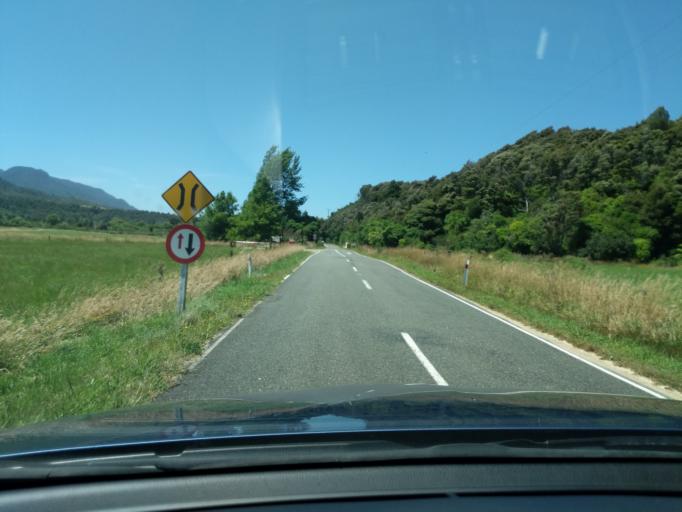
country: NZ
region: Tasman
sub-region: Tasman District
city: Takaka
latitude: -40.7284
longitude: 172.5839
